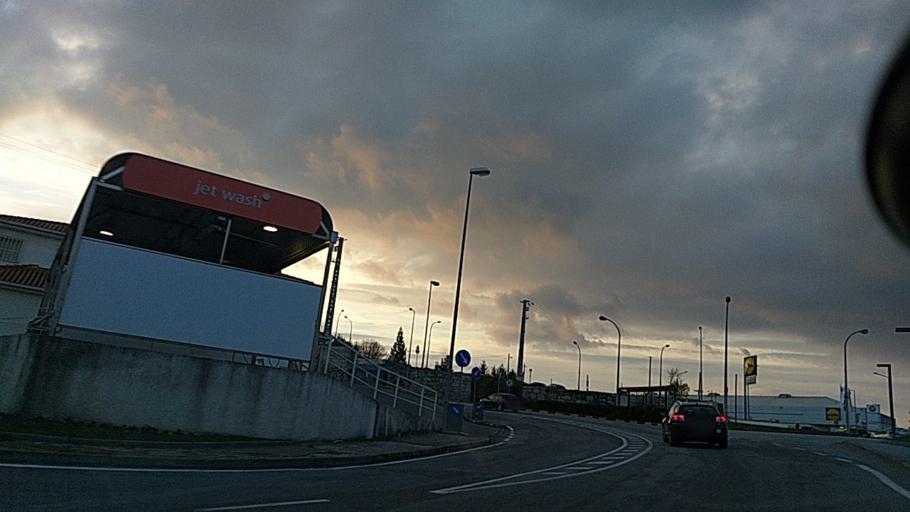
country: PT
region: Guarda
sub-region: Guarda
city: Guarda
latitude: 40.5433
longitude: -7.2576
